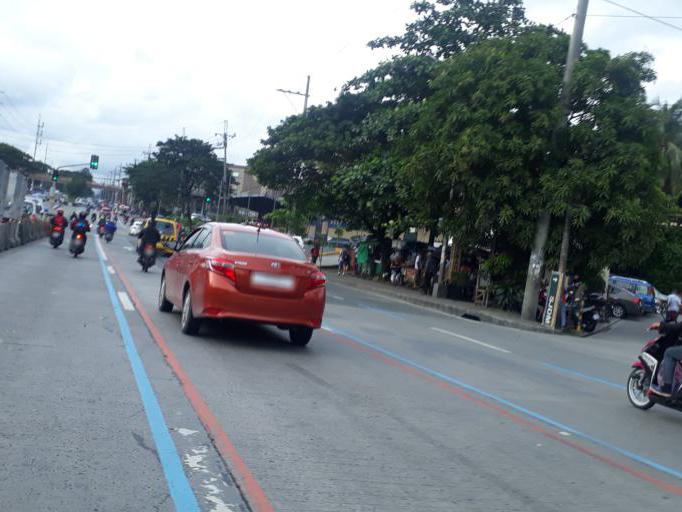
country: PH
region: Metro Manila
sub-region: Quezon City
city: Quezon City
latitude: 14.6475
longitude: 121.0745
